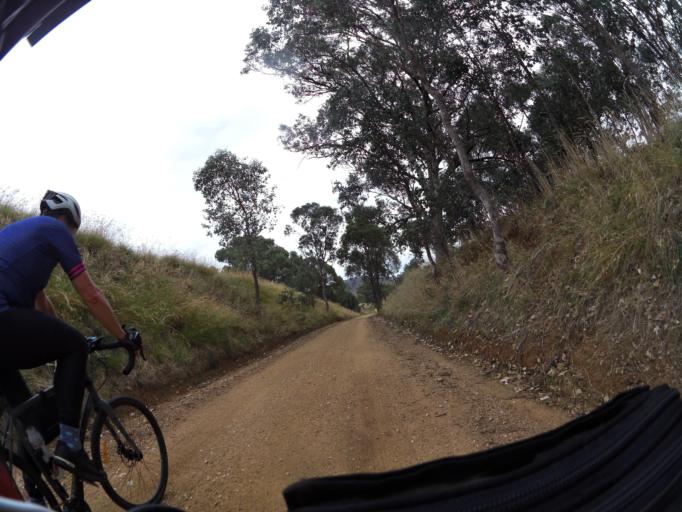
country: AU
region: New South Wales
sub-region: Albury Municipality
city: East Albury
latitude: -36.2006
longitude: 147.0449
